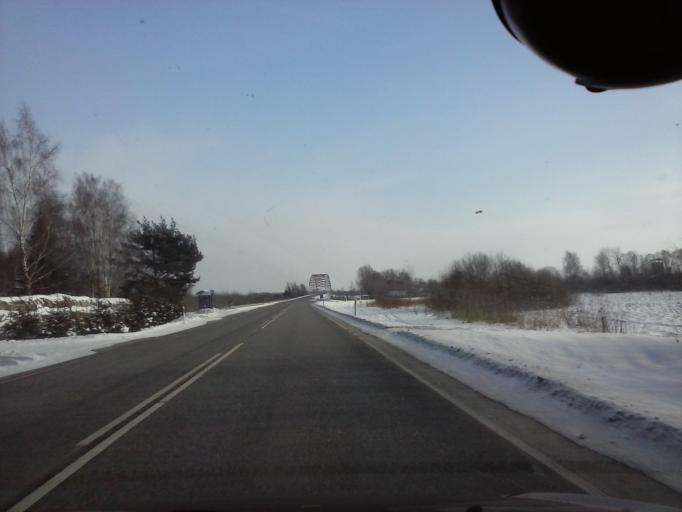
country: EE
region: Tartu
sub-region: Puhja vald
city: Puhja
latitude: 58.3894
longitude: 26.1291
